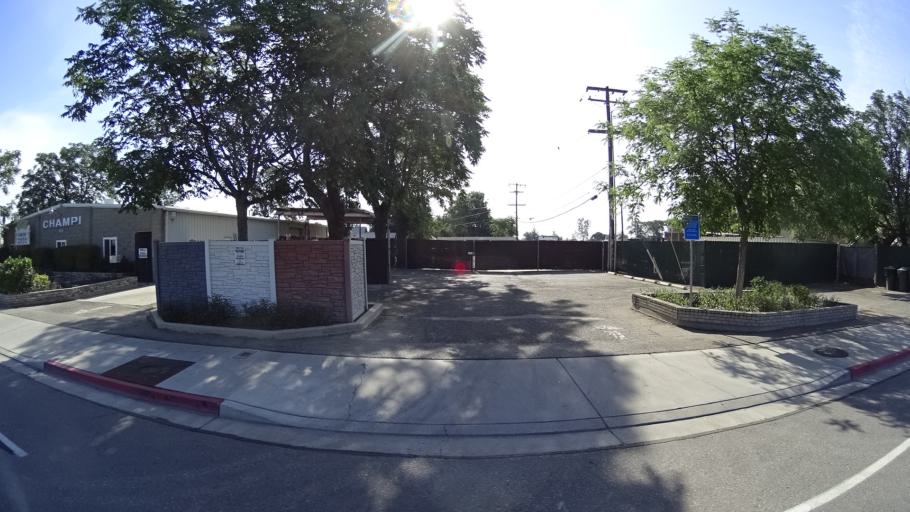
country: US
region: California
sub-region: Kings County
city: Hanford
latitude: 36.3318
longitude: -119.6370
